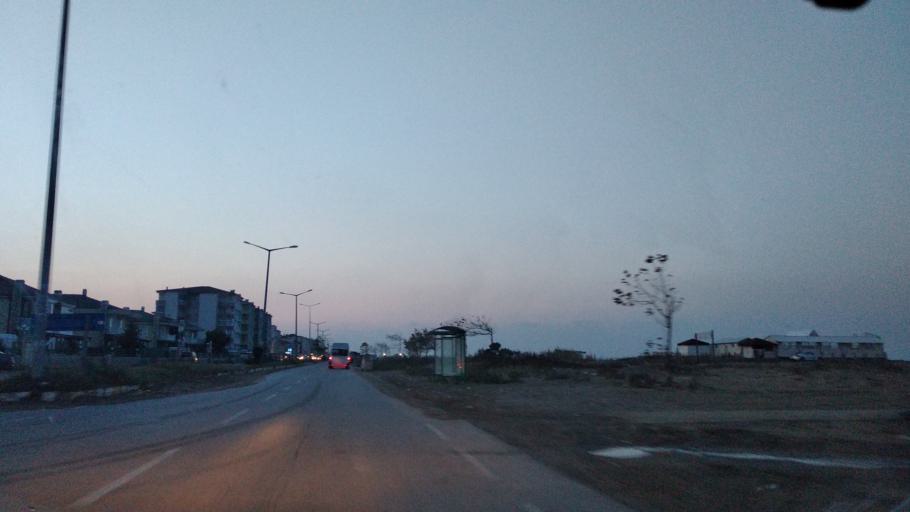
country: TR
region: Sakarya
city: Karasu
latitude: 41.0993
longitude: 30.7224
